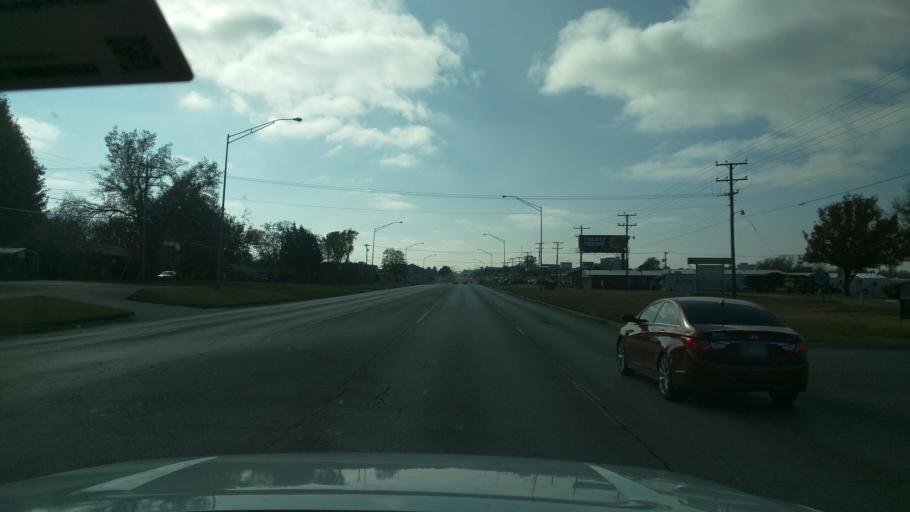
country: US
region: Oklahoma
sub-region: Washington County
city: Dewey
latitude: 36.7644
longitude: -95.9355
